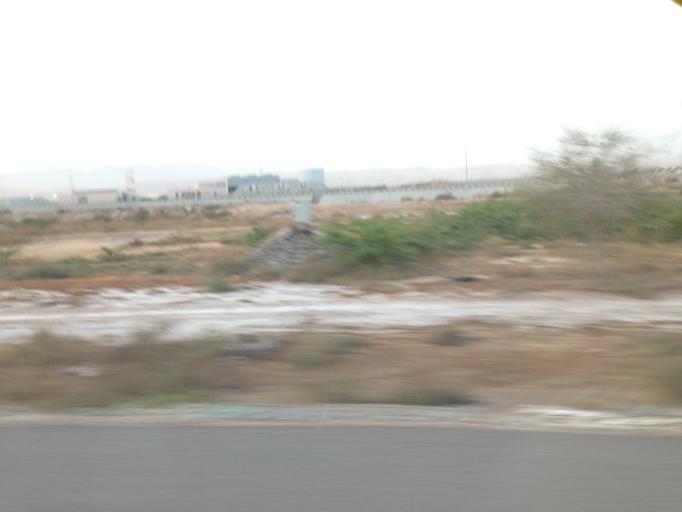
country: OM
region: Muhafazat Masqat
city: As Sib al Jadidah
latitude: 23.6203
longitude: 58.2732
